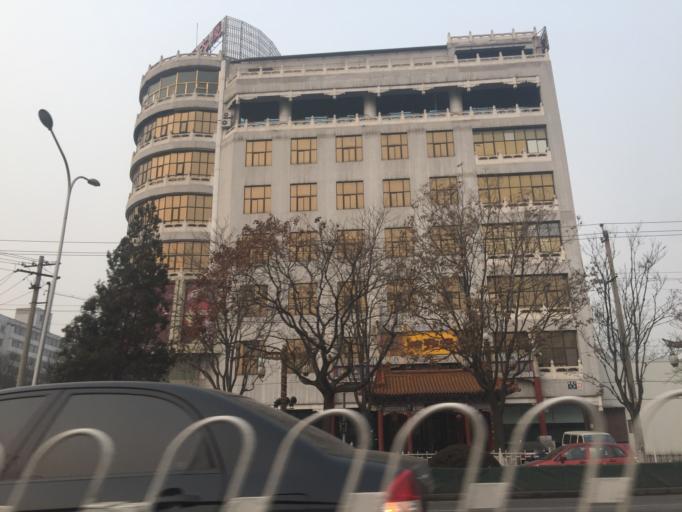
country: CN
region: Beijing
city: Datun
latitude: 39.9622
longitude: 116.3887
